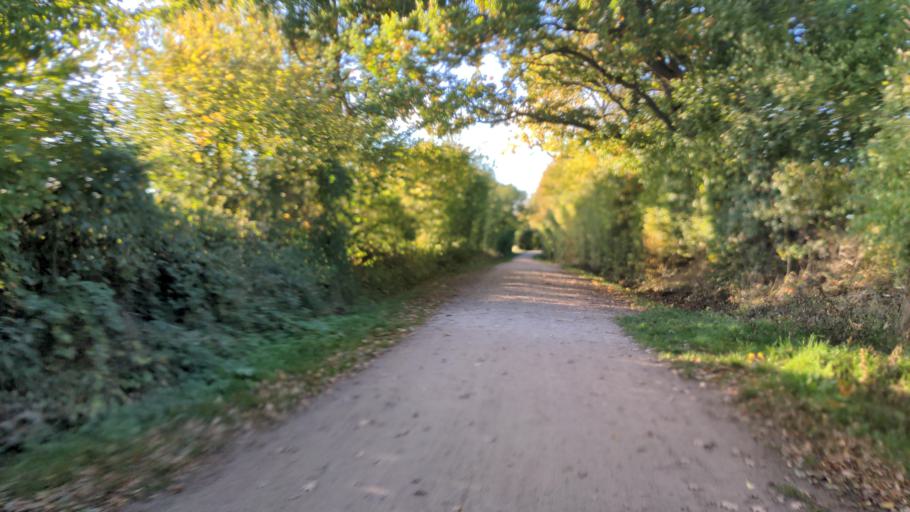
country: DE
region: Schleswig-Holstein
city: Neustadt in Holstein
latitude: 54.0943
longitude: 10.8416
